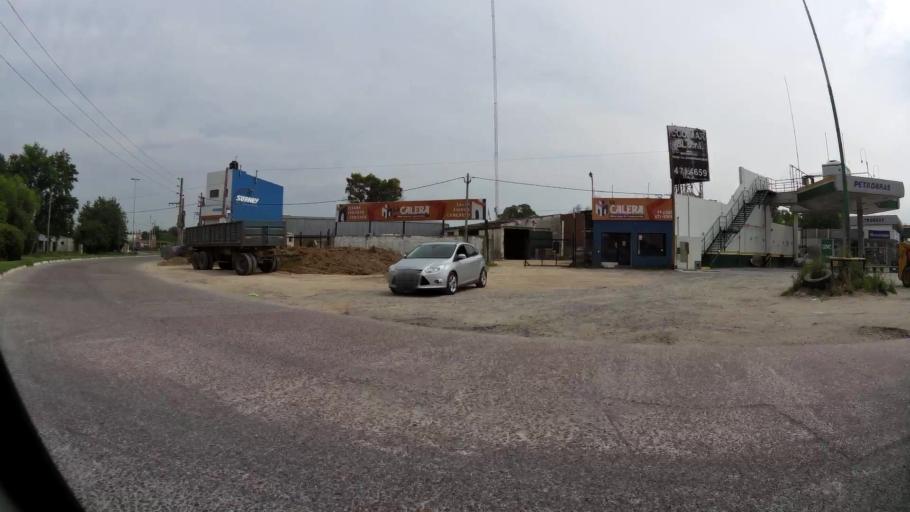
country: AR
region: Buenos Aires
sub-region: Partido de La Plata
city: La Plata
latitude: -34.9013
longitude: -57.9950
